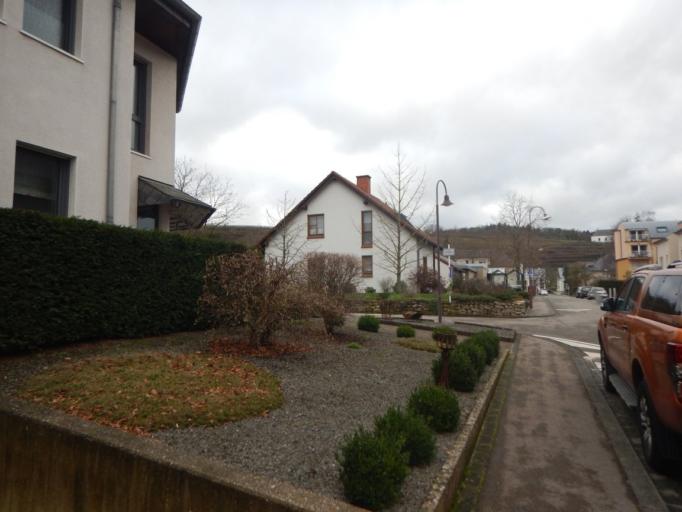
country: LU
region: Grevenmacher
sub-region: Canton de Grevenmacher
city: Grevenmacher
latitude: 49.6760
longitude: 6.4400
